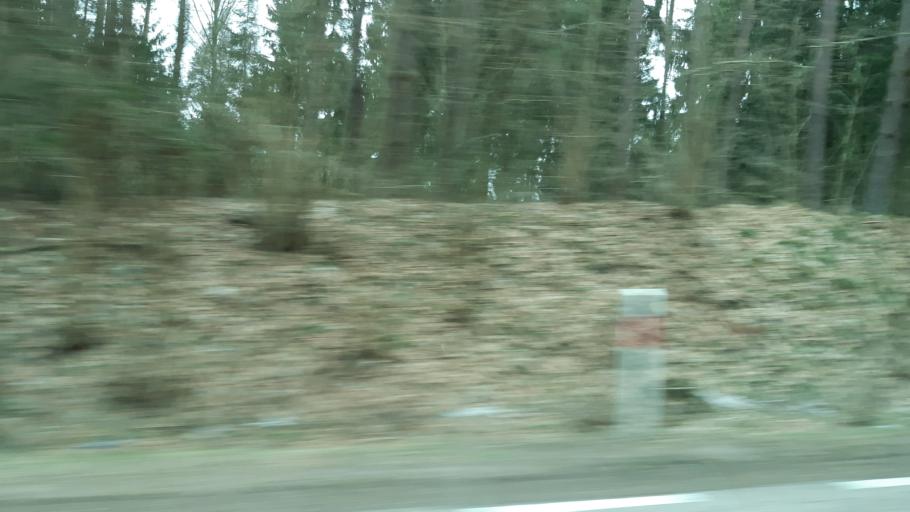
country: PL
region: Podlasie
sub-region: Suwalki
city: Suwalki
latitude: 54.3035
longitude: 22.9589
